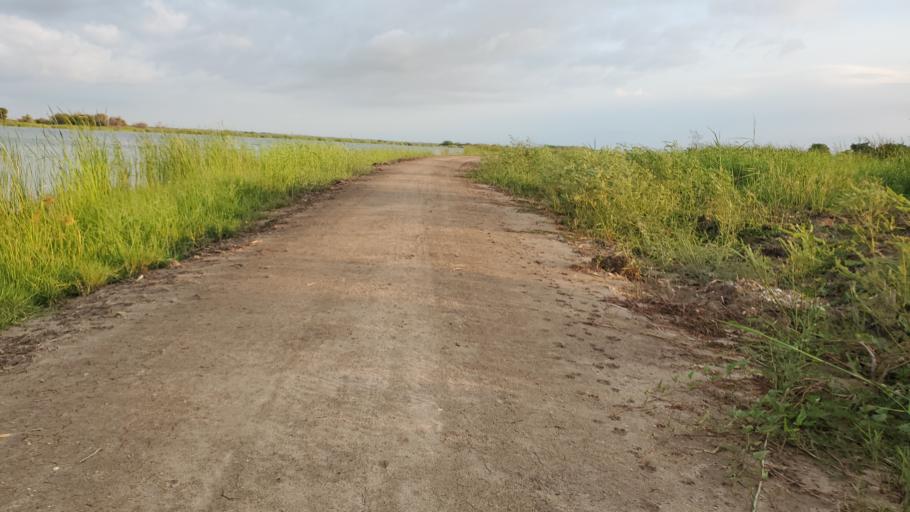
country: SN
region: Saint-Louis
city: Saint-Louis
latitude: 16.0159
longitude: -16.4007
